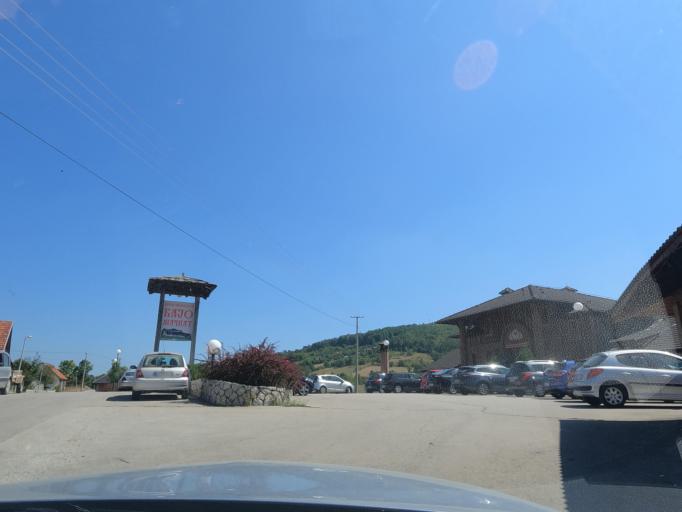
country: RS
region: Central Serbia
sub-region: Zlatiborski Okrug
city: Cajetina
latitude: 43.7886
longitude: 19.7683
